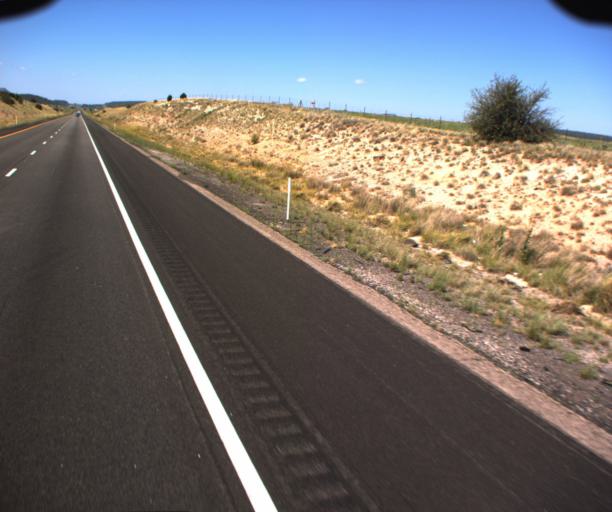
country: US
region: Arizona
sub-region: Mohave County
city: Peach Springs
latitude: 35.2667
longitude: -113.1524
